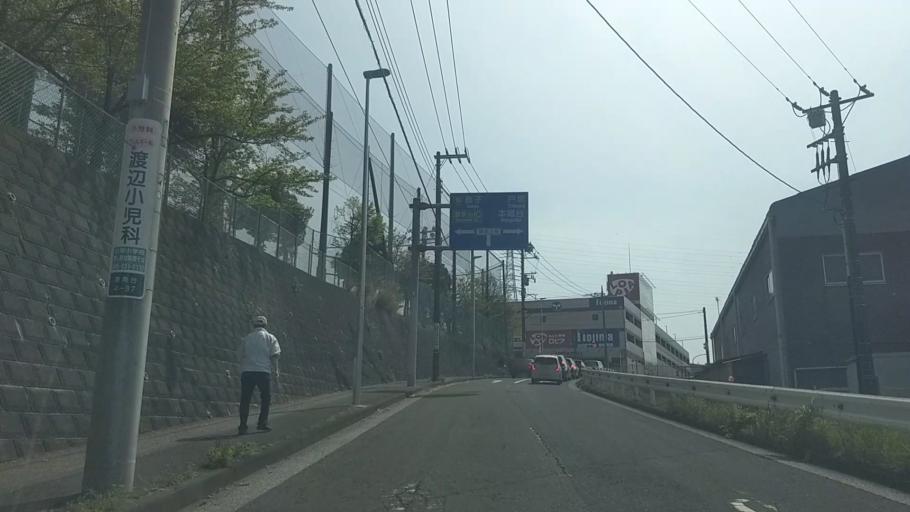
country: JP
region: Kanagawa
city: Kamakura
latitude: 35.3763
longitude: 139.5681
